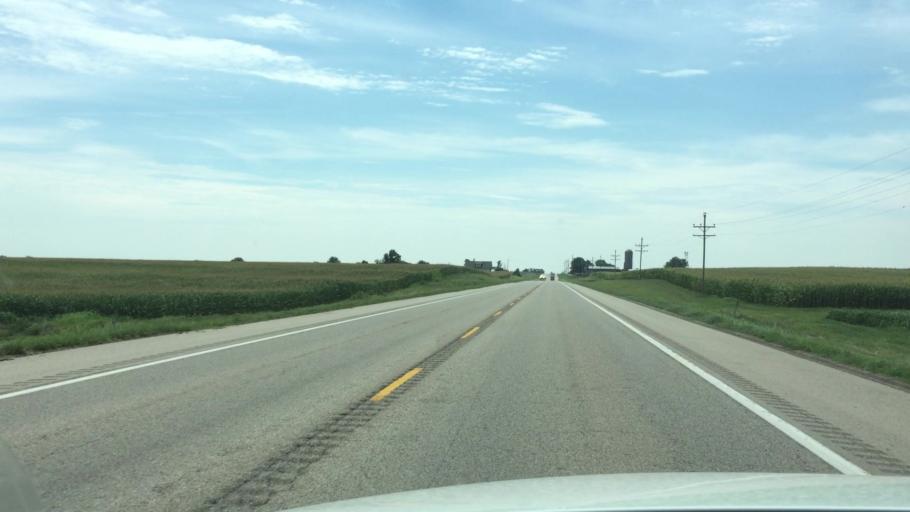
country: US
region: Kansas
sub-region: Nemaha County
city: Sabetha
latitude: 39.7810
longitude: -95.7295
